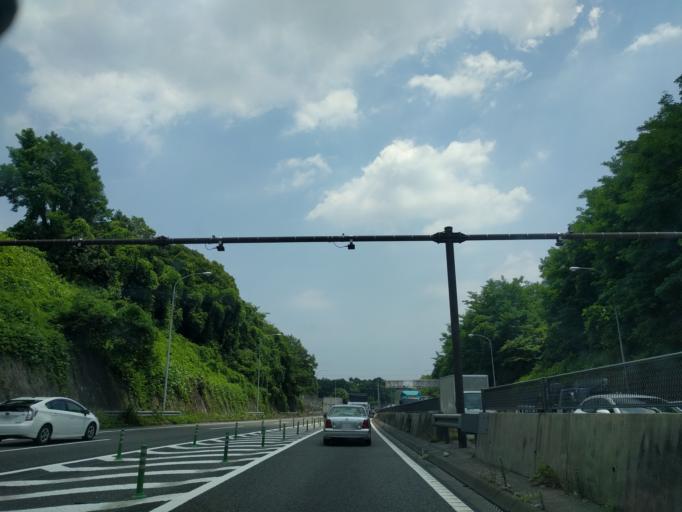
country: JP
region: Kanagawa
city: Minami-rinkan
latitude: 35.4949
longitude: 139.4982
